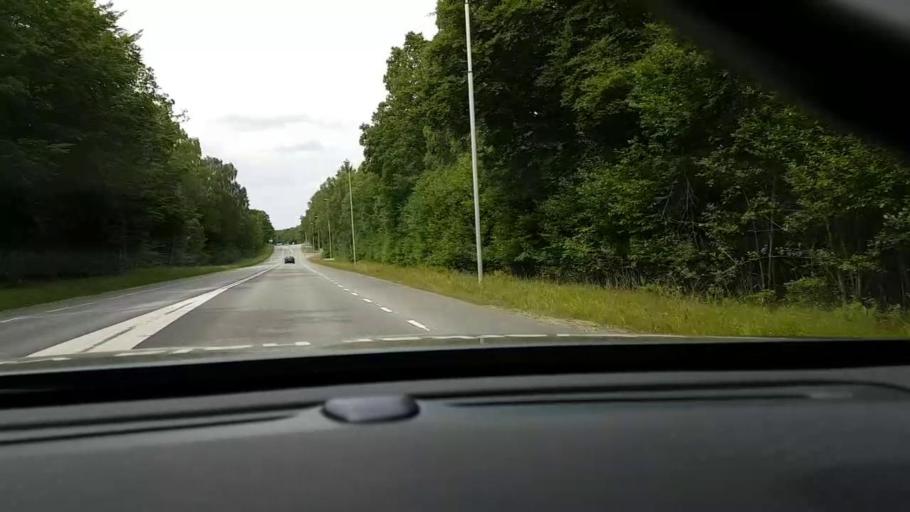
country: SE
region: Skane
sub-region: Hassleholms Kommun
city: Hassleholm
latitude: 56.1613
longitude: 13.7384
